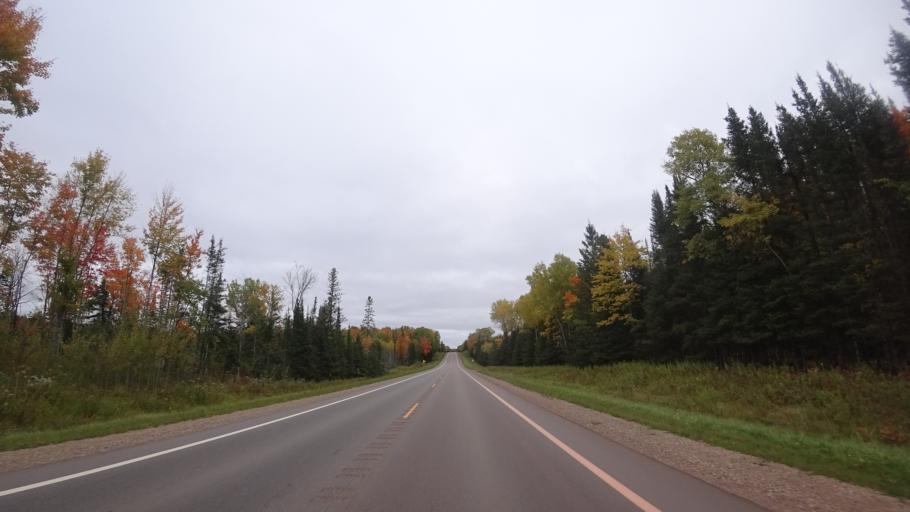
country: US
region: Michigan
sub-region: Iron County
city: Crystal Falls
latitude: 46.1521
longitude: -88.0880
